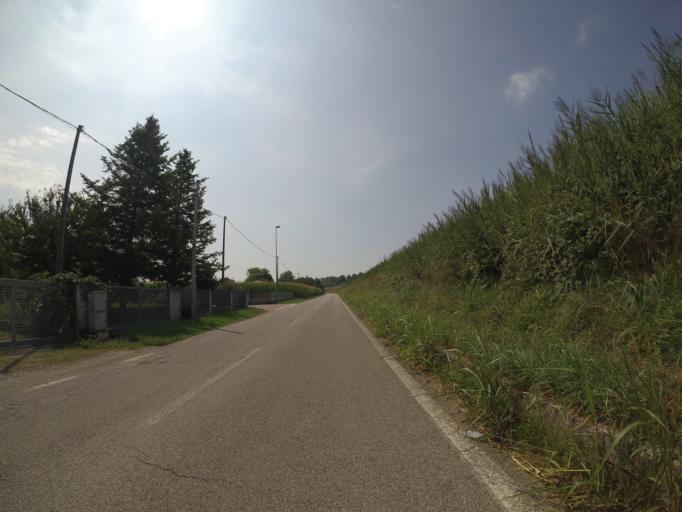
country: IT
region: Friuli Venezia Giulia
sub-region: Provincia di Udine
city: Pertegada
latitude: 45.7105
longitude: 13.0417
